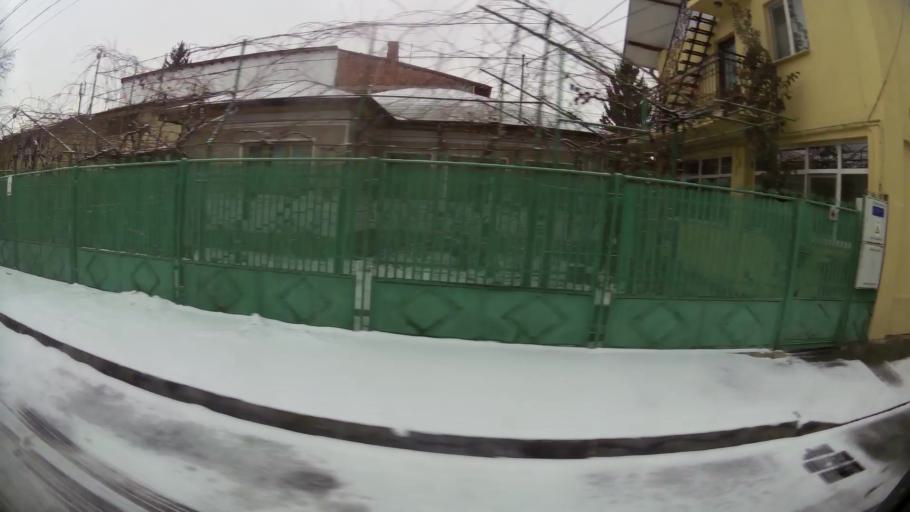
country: RO
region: Prahova
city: Ploiesti
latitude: 44.9276
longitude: 26.0150
